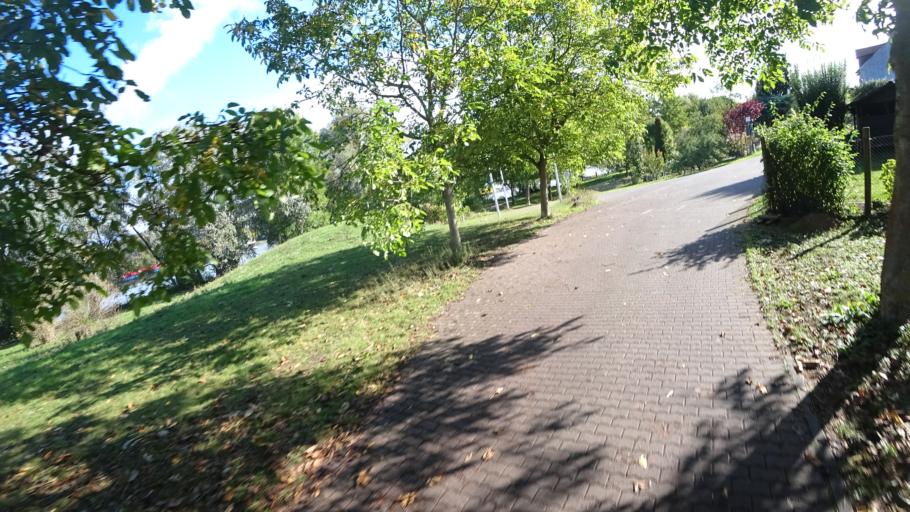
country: DE
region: Rheinland-Pfalz
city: Rhens
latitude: 50.2866
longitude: 7.6112
